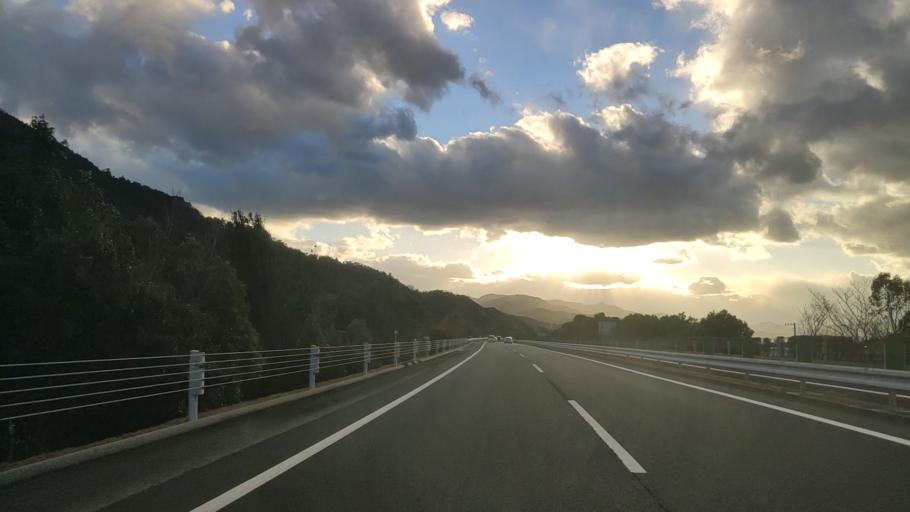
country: JP
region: Ehime
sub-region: Shikoku-chuo Shi
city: Matsuyama
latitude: 33.7920
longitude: 132.8977
